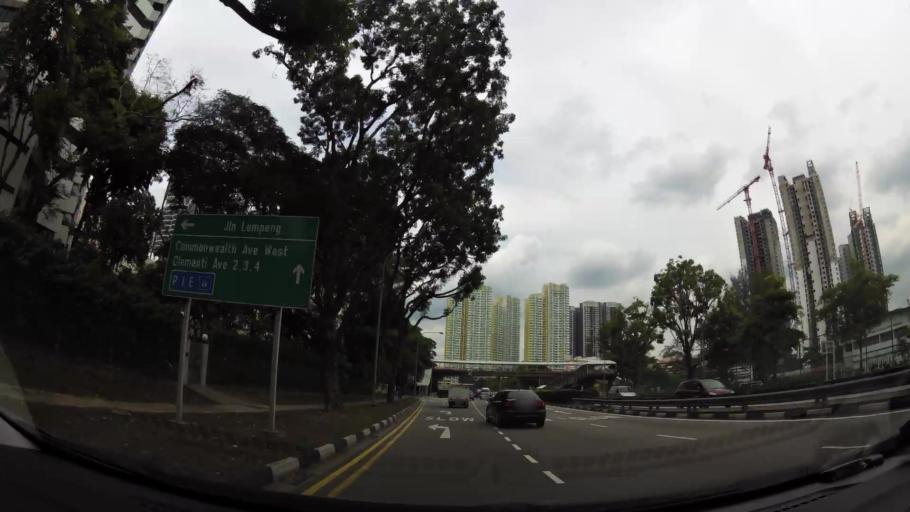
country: SG
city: Singapore
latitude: 1.3161
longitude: 103.7610
